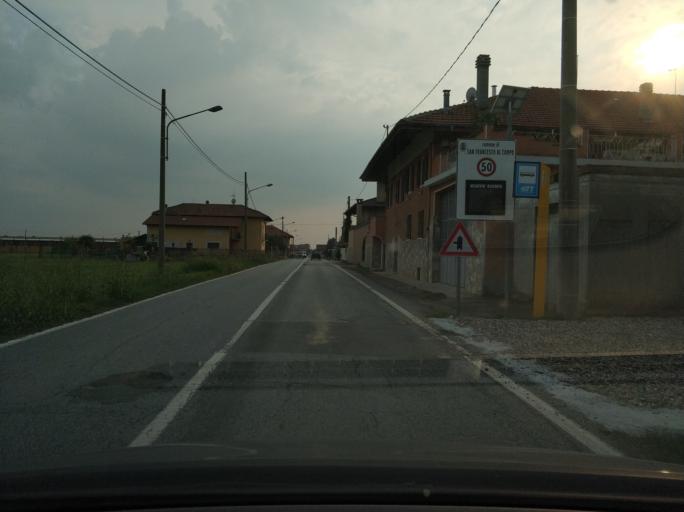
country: IT
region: Piedmont
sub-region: Provincia di Torino
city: San Francesco al Campo
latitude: 45.2367
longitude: 7.6526
